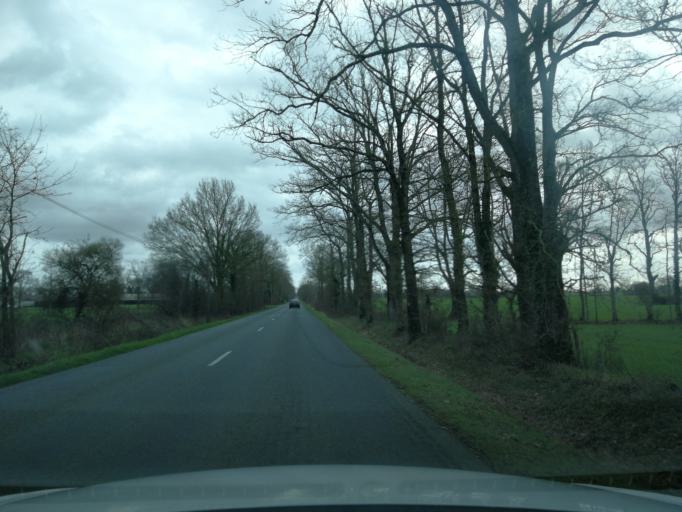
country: FR
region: Pays de la Loire
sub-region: Departement de la Loire-Atlantique
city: Montbert
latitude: 47.0161
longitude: -1.4842
